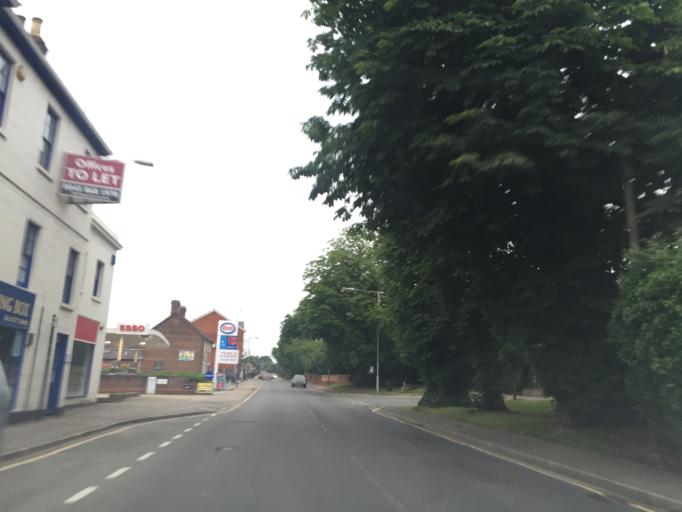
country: GB
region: England
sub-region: Essex
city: Chipping Ongar
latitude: 51.7065
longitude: 0.2451
